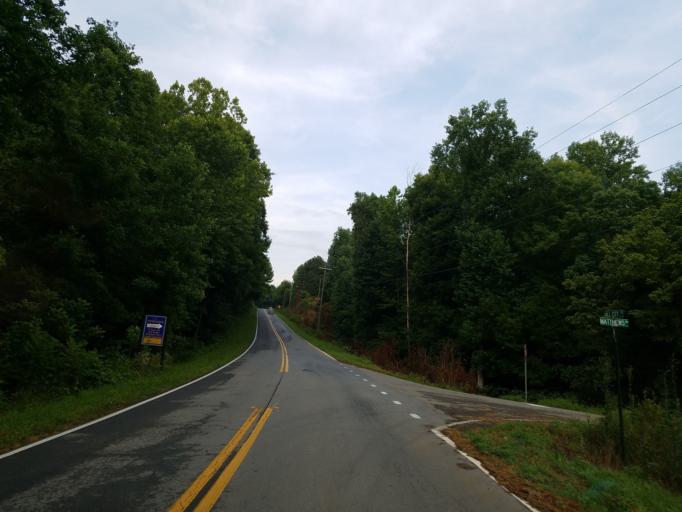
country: US
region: Georgia
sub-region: Pickens County
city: Jasper
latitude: 34.4519
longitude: -84.5527
